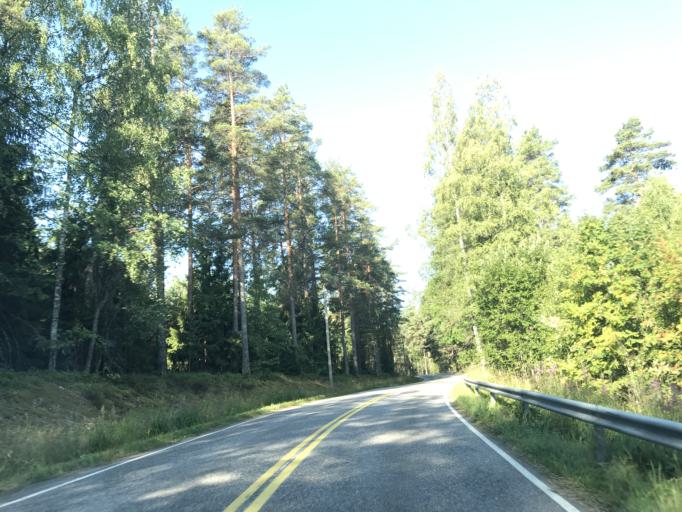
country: FI
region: Uusimaa
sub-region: Helsinki
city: Lohja
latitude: 60.2811
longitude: 24.1351
